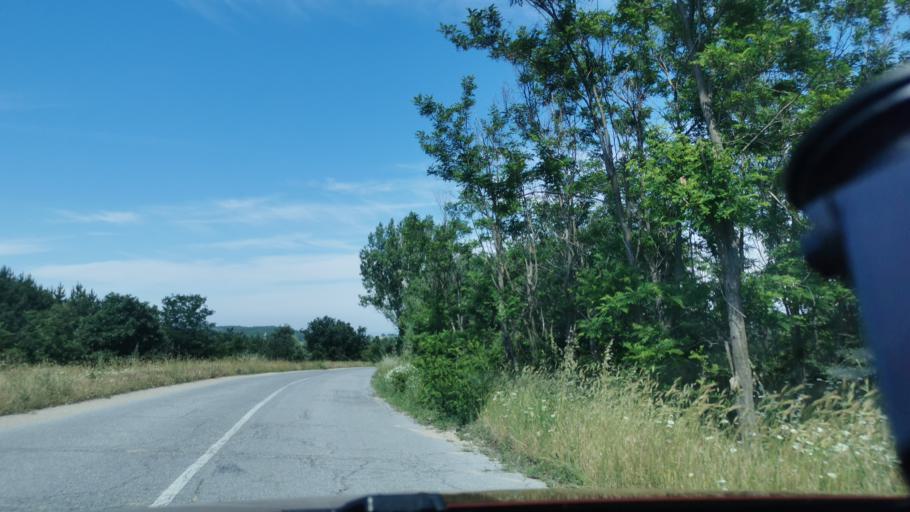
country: BG
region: Khaskovo
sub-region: Obshtina Topolovgrad
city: Topolovgrad
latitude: 42.0404
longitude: 26.1350
